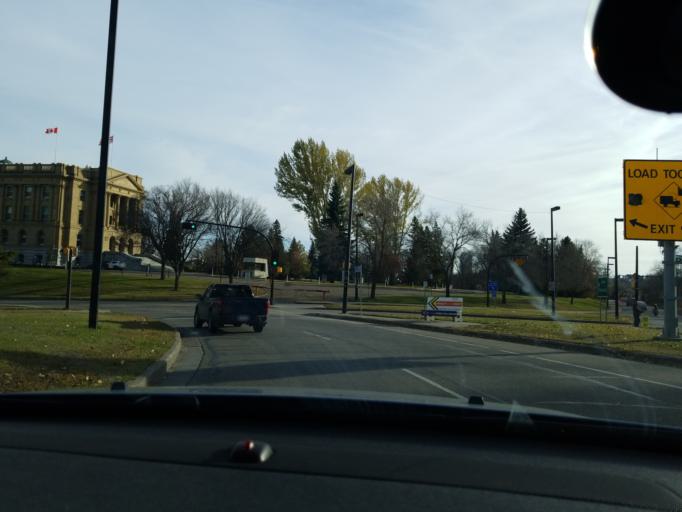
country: CA
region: Alberta
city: Edmonton
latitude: 53.5346
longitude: -113.5084
